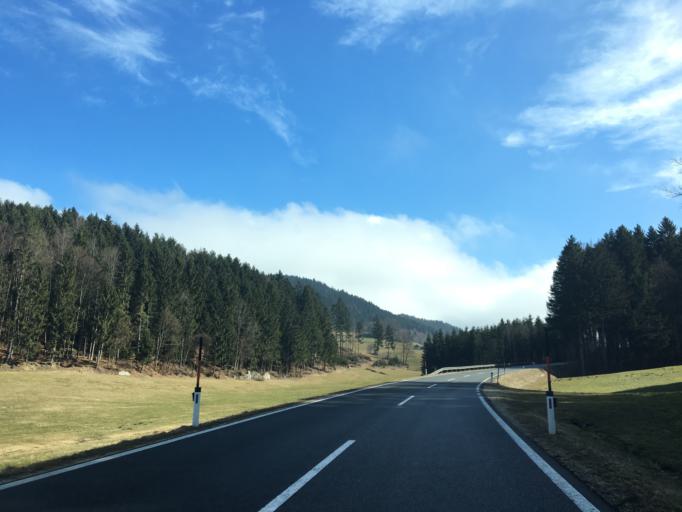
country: AT
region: Upper Austria
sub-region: Politischer Bezirk Perg
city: Sankt Georgen am Walde
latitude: 48.4192
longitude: 14.7955
